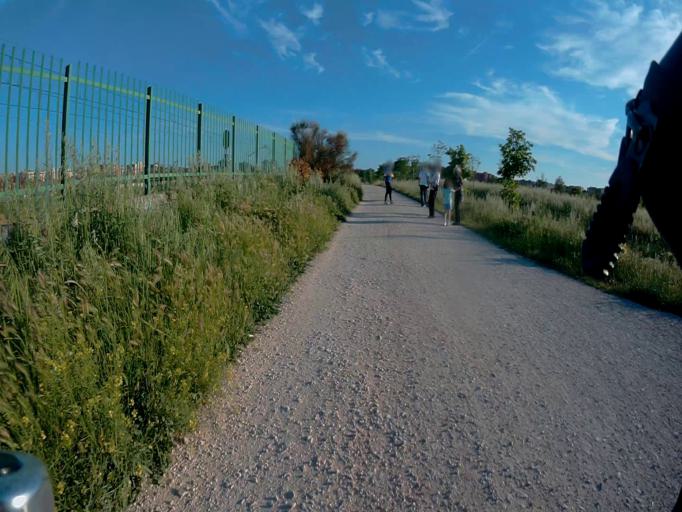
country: ES
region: Madrid
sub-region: Provincia de Madrid
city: Fuenlabrada
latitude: 40.3018
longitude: -3.7898
